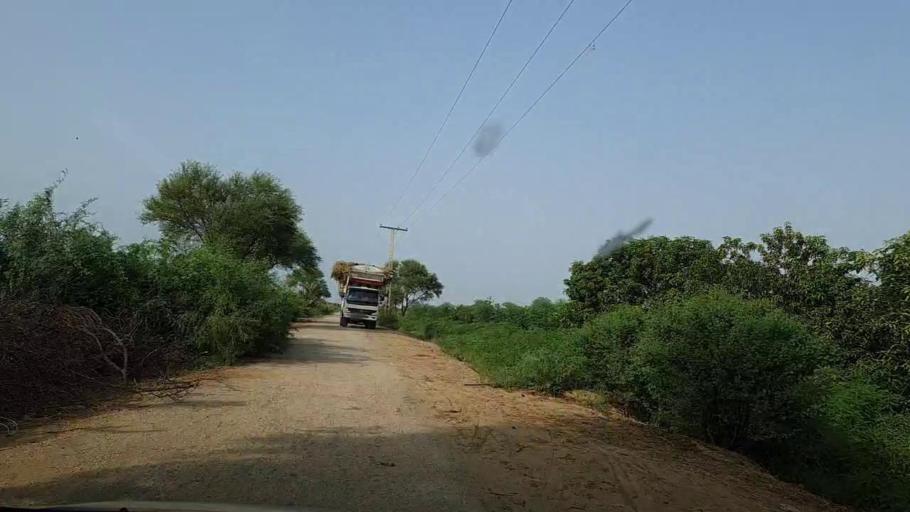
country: PK
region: Sindh
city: Kotri
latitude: 25.2277
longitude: 68.2543
